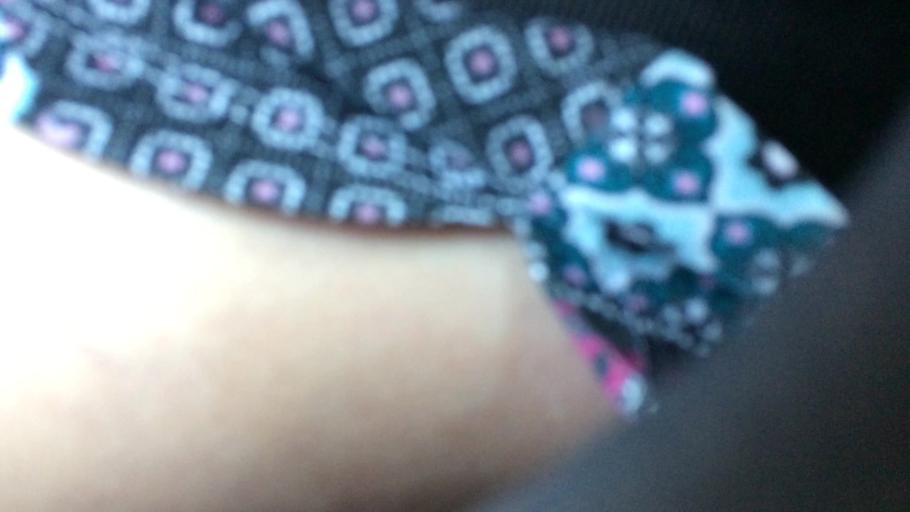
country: US
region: New Mexico
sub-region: San Miguel County
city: Las Vegas
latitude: 35.8651
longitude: -104.8835
